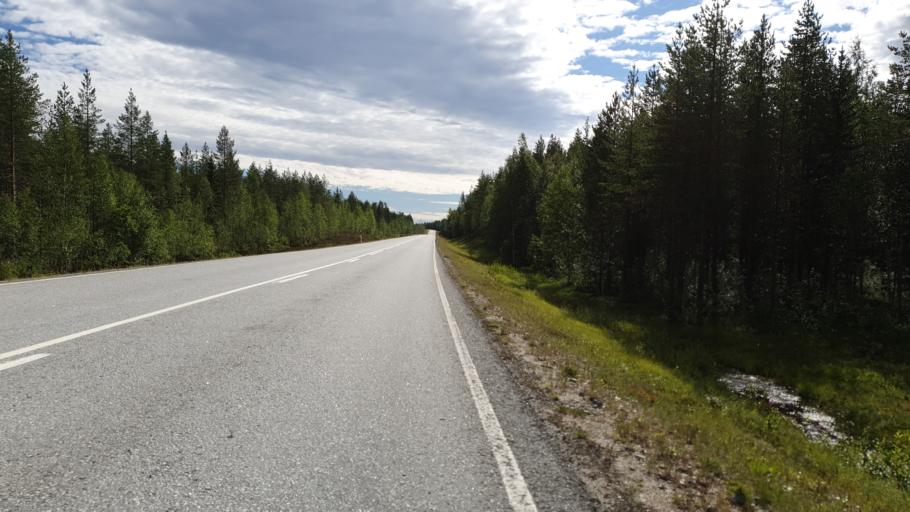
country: FI
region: Kainuu
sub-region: Kehys-Kainuu
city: Kuhmo
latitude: 64.4913
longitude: 29.8377
